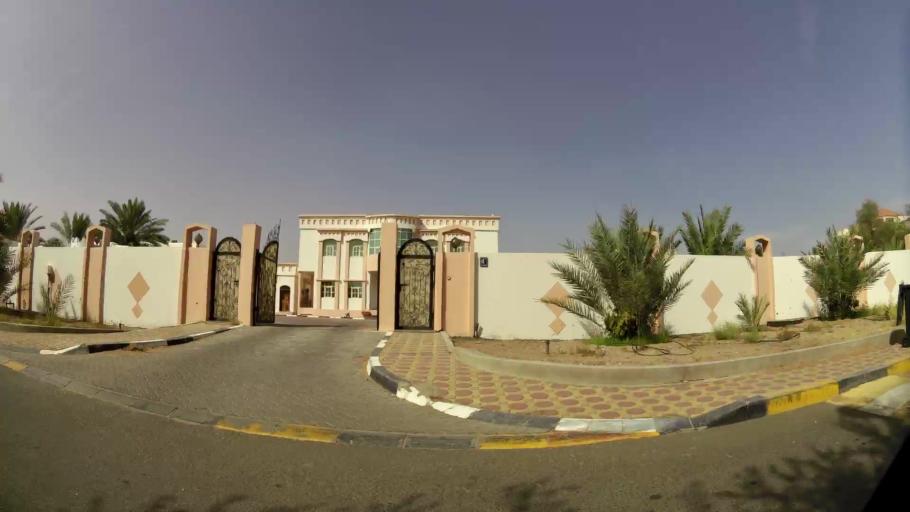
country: AE
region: Abu Dhabi
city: Al Ain
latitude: 24.2460
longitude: 55.6853
